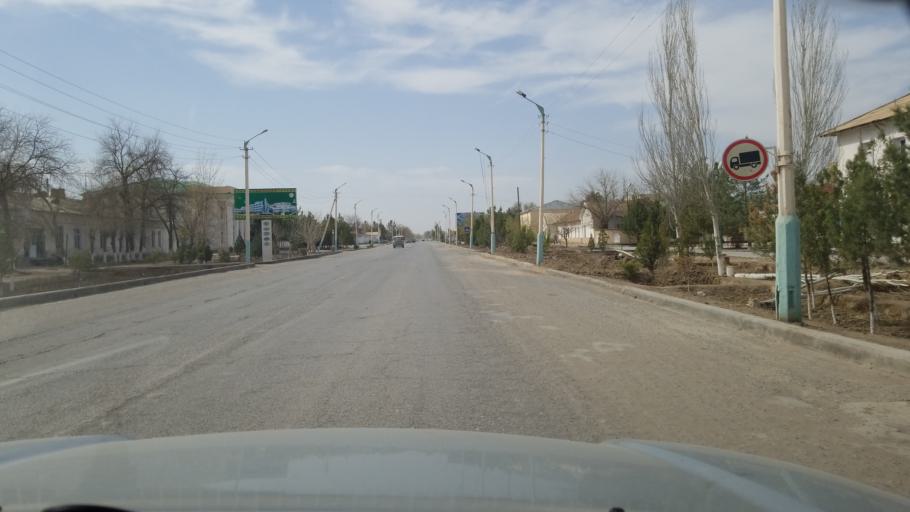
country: TM
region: Lebap
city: Atamyrat
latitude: 37.8395
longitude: 65.2088
